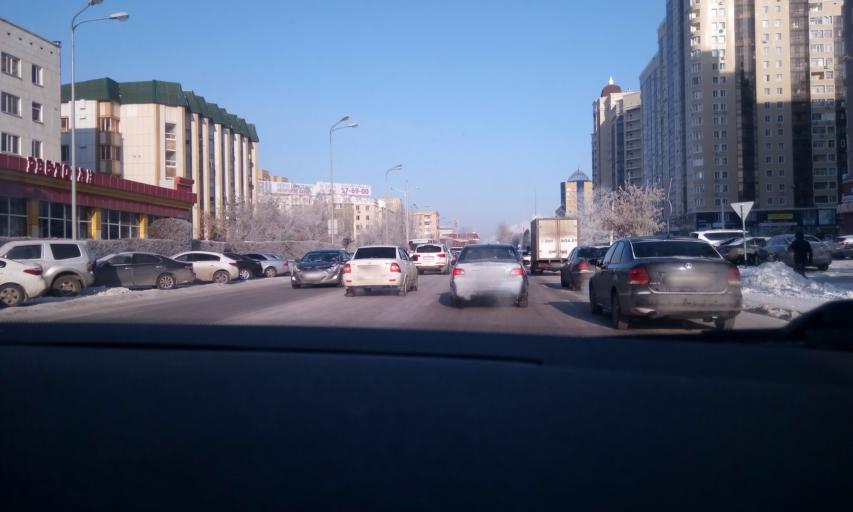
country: KZ
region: Astana Qalasy
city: Astana
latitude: 51.1659
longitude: 71.4403
